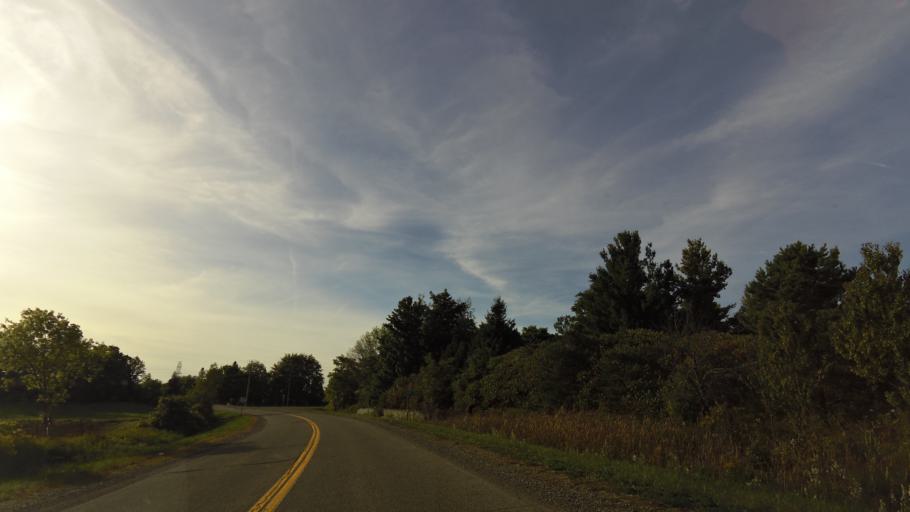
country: CA
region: Ontario
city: Ancaster
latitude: 43.1686
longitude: -79.9536
